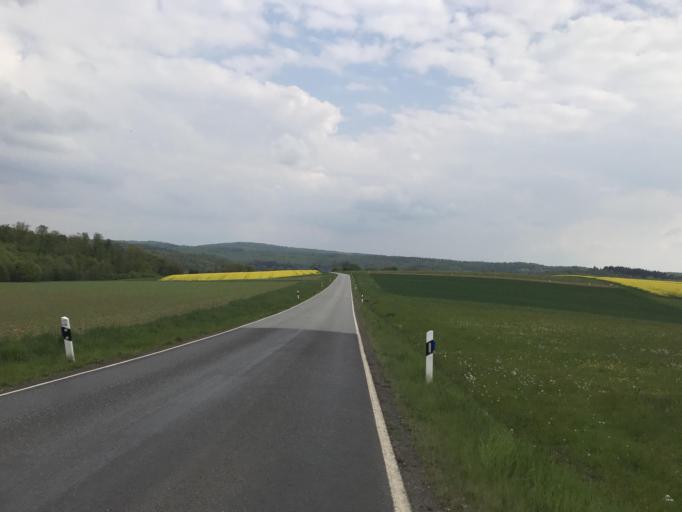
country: DE
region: Hesse
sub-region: Regierungsbezirk Giessen
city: Laubach
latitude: 50.5223
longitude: 9.0104
